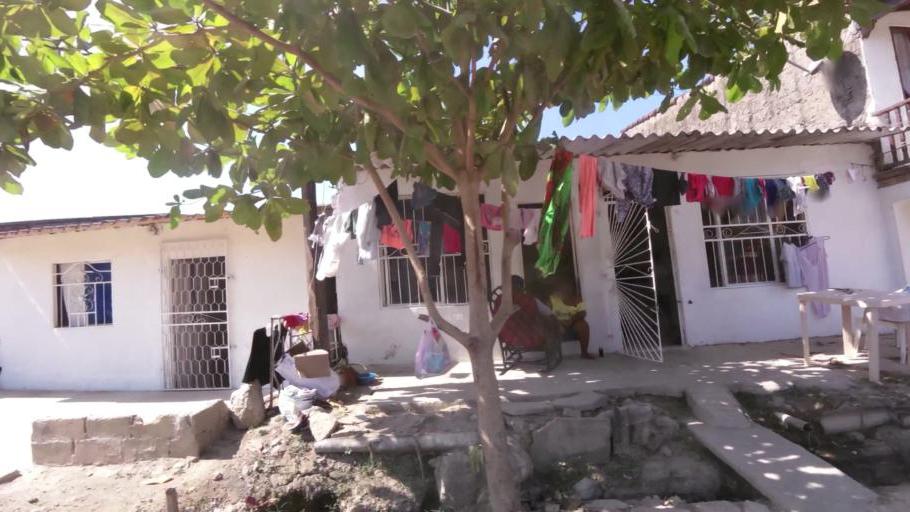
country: CO
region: Bolivar
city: Cartagena
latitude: 10.3737
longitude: -75.4672
